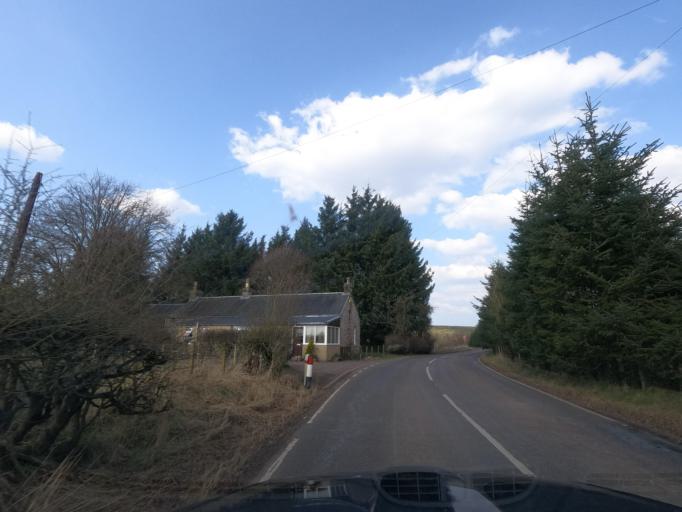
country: GB
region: Scotland
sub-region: South Lanarkshire
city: Forth
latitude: 55.7627
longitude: -3.6678
